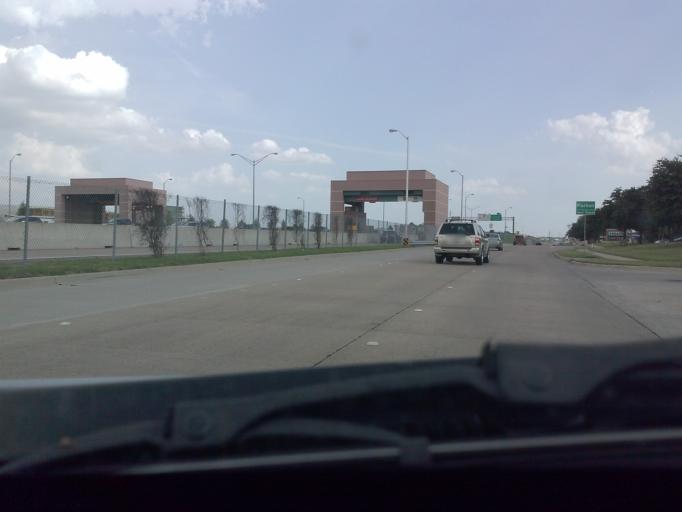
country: US
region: Texas
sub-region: Denton County
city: The Colony
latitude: 33.0491
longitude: -96.8302
